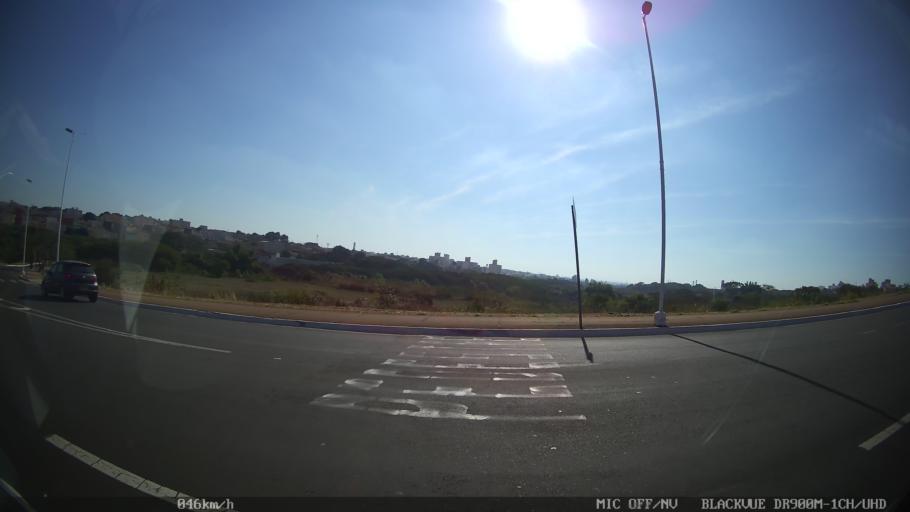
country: BR
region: Sao Paulo
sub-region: Sao Jose Do Rio Preto
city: Sao Jose do Rio Preto
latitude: -20.8031
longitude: -49.4056
